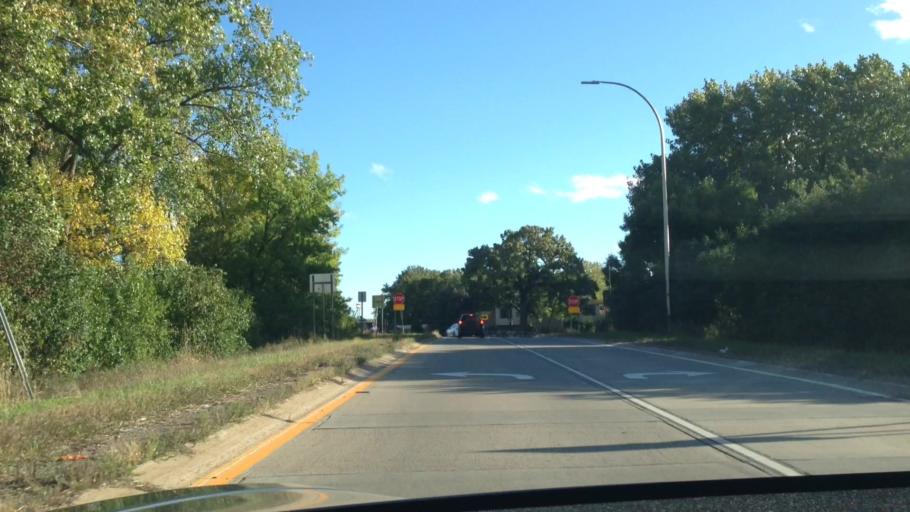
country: US
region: Minnesota
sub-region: Hennepin County
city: Minnetonka Mills
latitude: 44.9406
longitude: -93.3987
